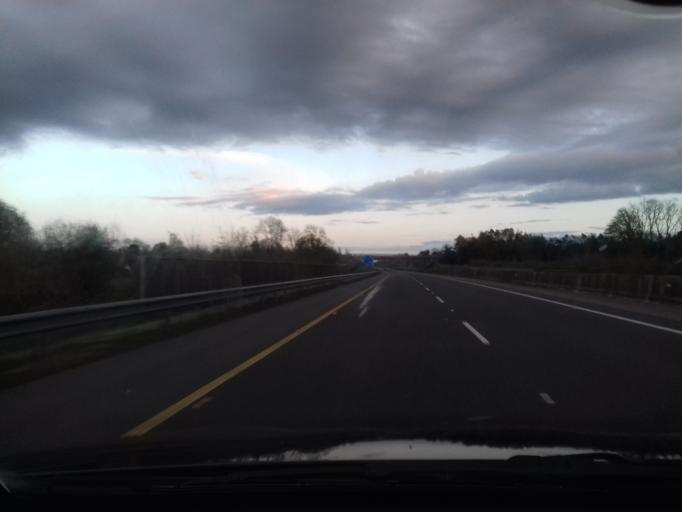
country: IE
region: Leinster
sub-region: An Mhi
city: Navan
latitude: 53.6508
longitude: -6.7517
